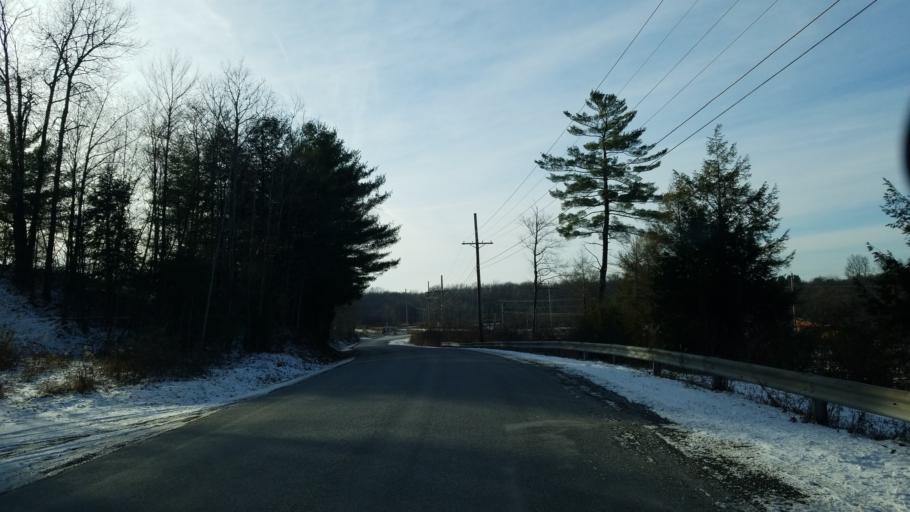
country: US
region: Pennsylvania
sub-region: Clearfield County
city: DuBois
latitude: 41.1210
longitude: -78.7140
